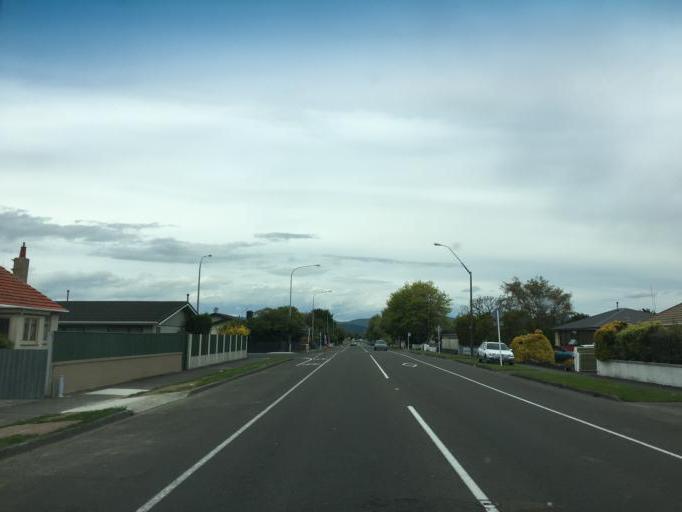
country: NZ
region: Manawatu-Wanganui
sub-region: Palmerston North City
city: Palmerston North
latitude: -40.3595
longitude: 175.5914
